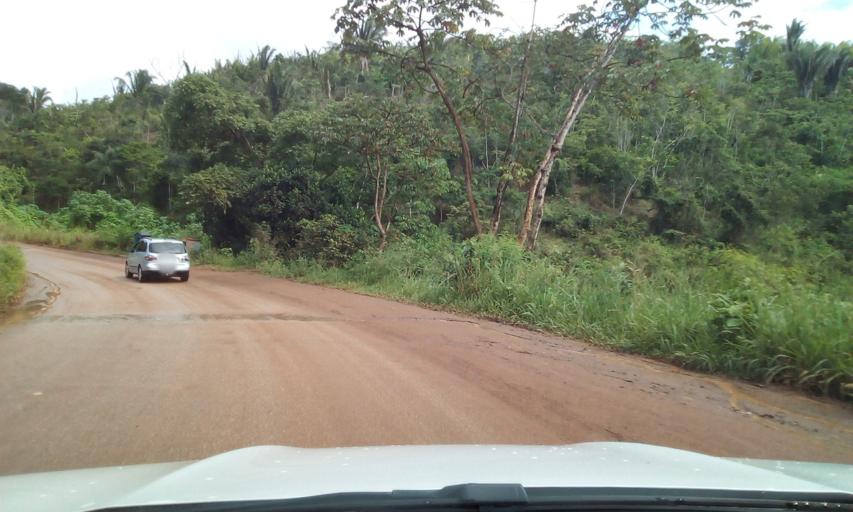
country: BR
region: Paraiba
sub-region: Areia
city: Areia
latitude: -6.9561
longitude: -35.6842
